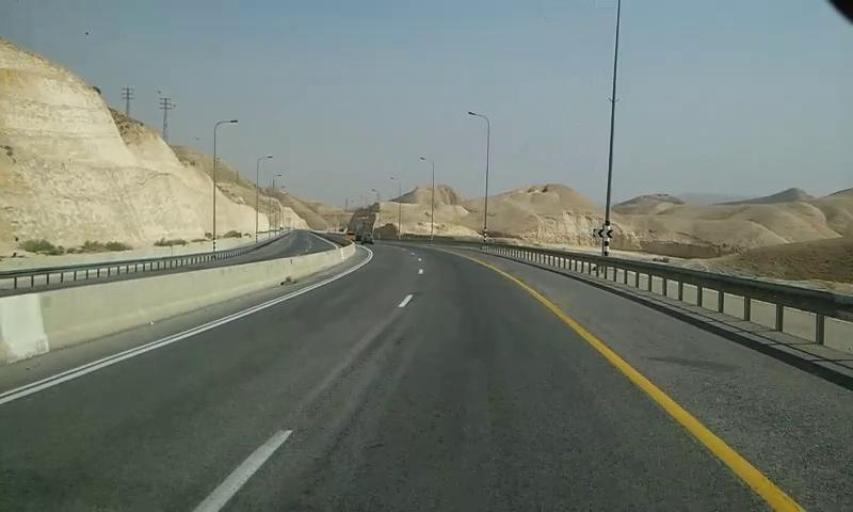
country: PS
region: West Bank
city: Jericho
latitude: 31.8084
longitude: 35.3940
